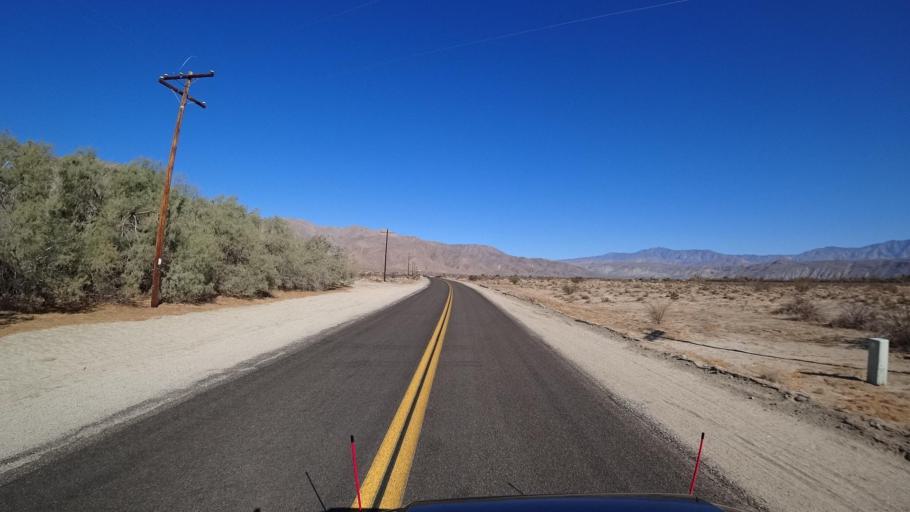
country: US
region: California
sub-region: San Diego County
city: Borrego Springs
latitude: 33.2941
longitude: -116.3790
